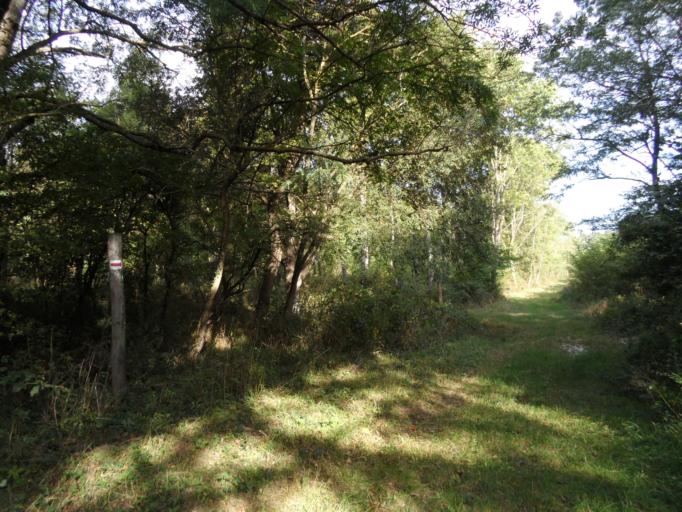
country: HU
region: Veszprem
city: Devecser
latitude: 47.2048
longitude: 17.4552
